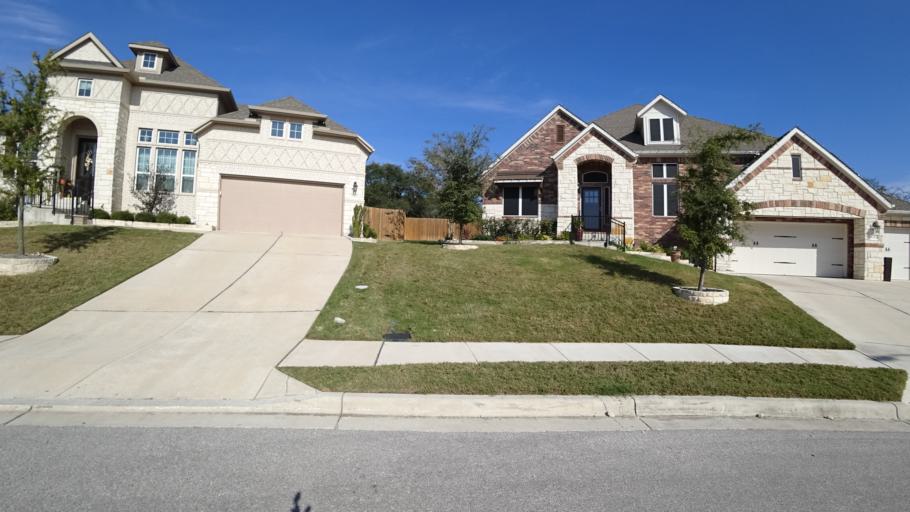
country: US
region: Texas
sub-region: Travis County
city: Barton Creek
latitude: 30.2325
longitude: -97.9061
